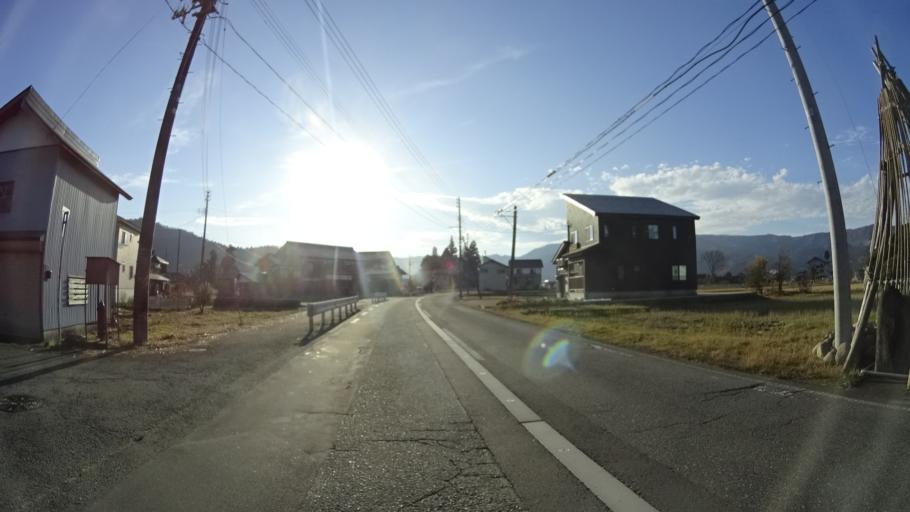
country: JP
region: Niigata
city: Shiozawa
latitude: 37.0087
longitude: 138.8469
